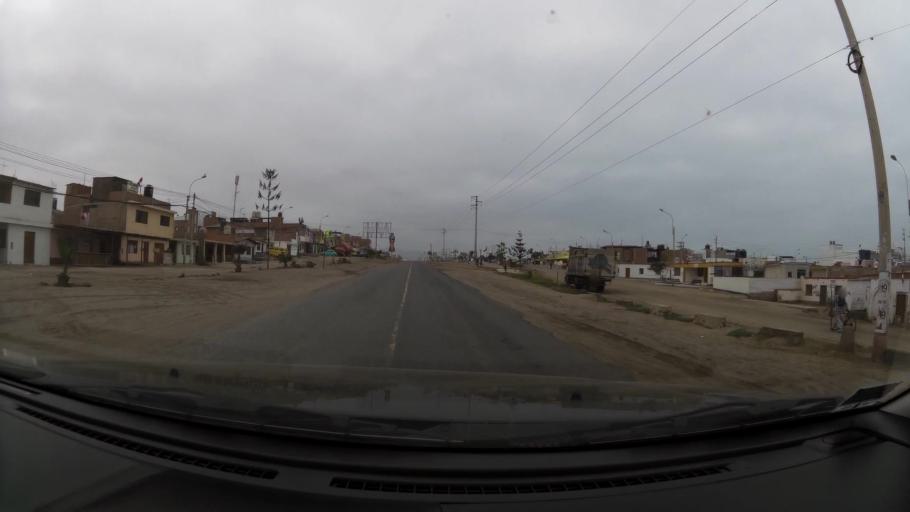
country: PE
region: Lima
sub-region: Lima
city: San Bartolo
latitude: -12.3632
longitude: -76.7959
